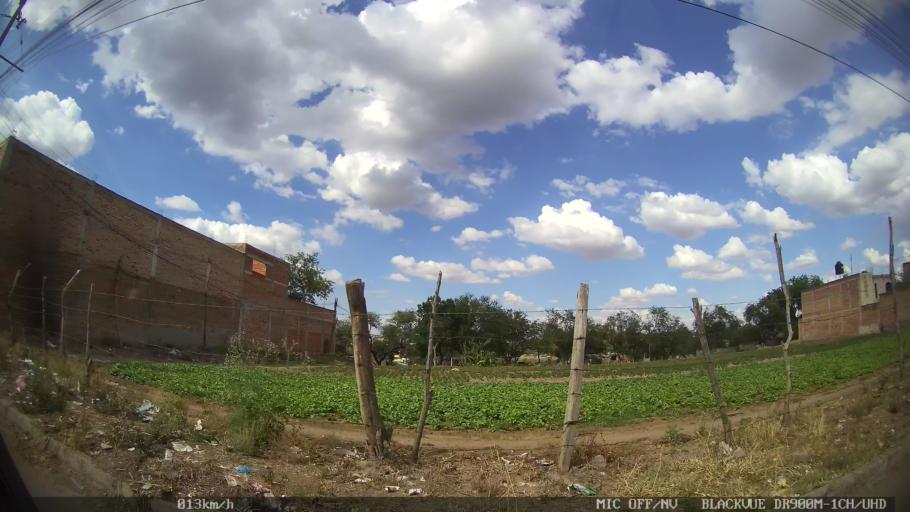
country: MX
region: Jalisco
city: Tlaquepaque
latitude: 20.6642
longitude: -103.2639
